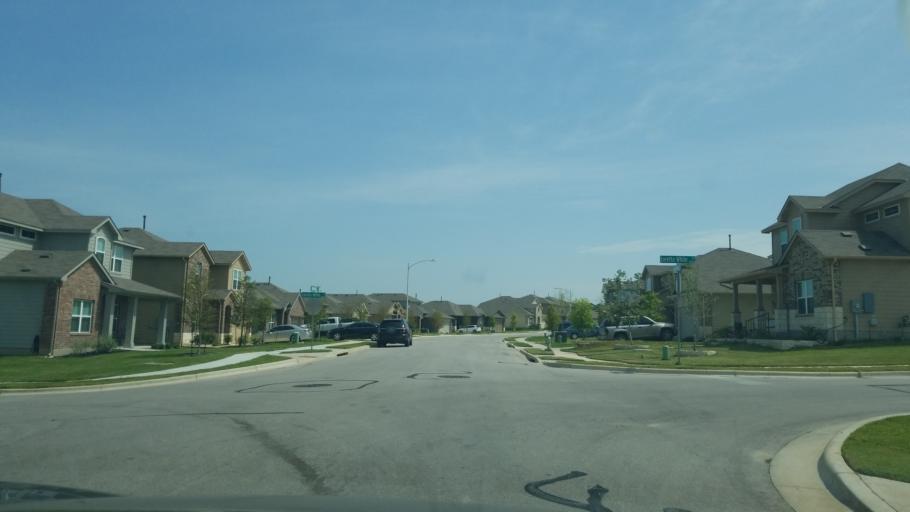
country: US
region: Texas
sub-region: Travis County
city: Onion Creek
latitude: 30.1697
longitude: -97.7299
